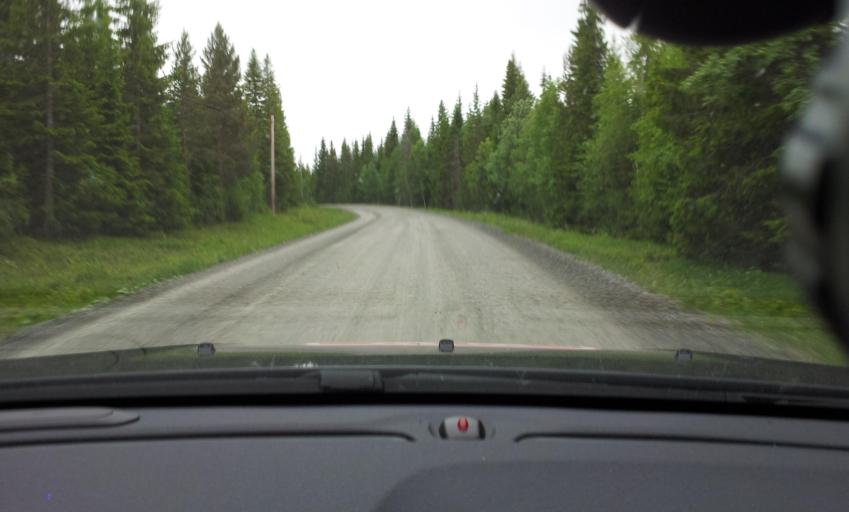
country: SE
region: Jaemtland
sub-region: Are Kommun
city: Jarpen
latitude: 63.2867
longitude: 13.6432
